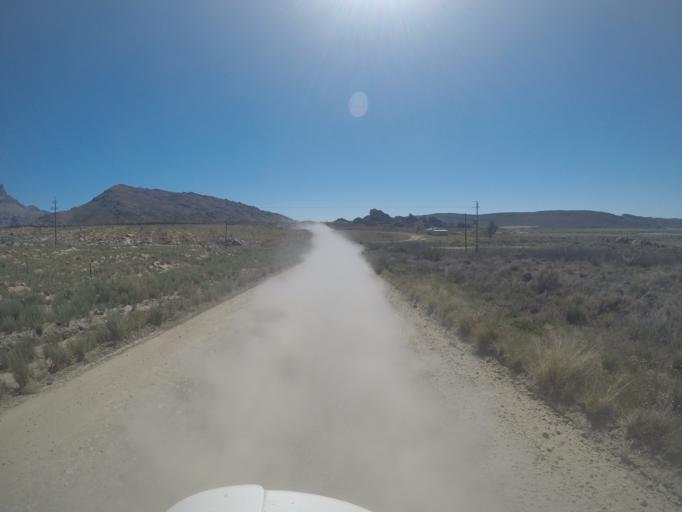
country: ZA
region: Western Cape
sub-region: Cape Winelands District Municipality
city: Ceres
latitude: -32.8614
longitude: 19.4434
